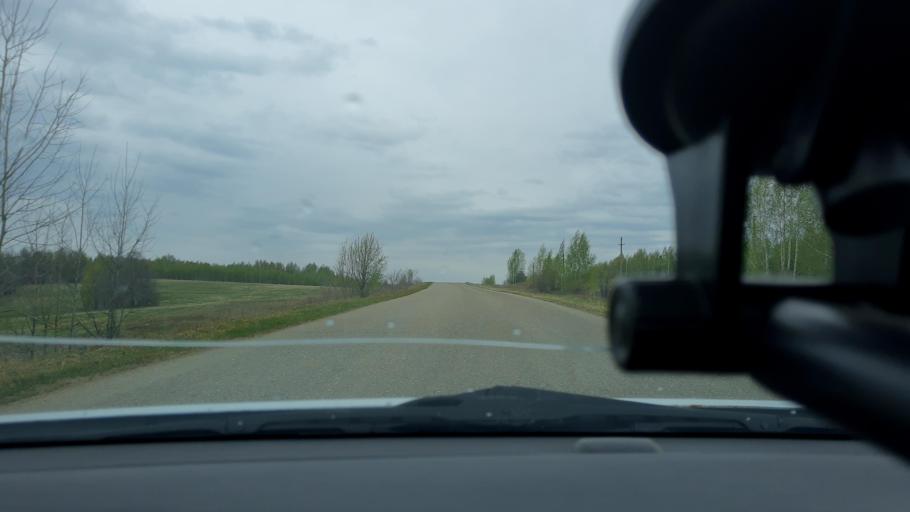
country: RU
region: Bashkortostan
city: Pavlovka
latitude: 55.3702
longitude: 56.4223
